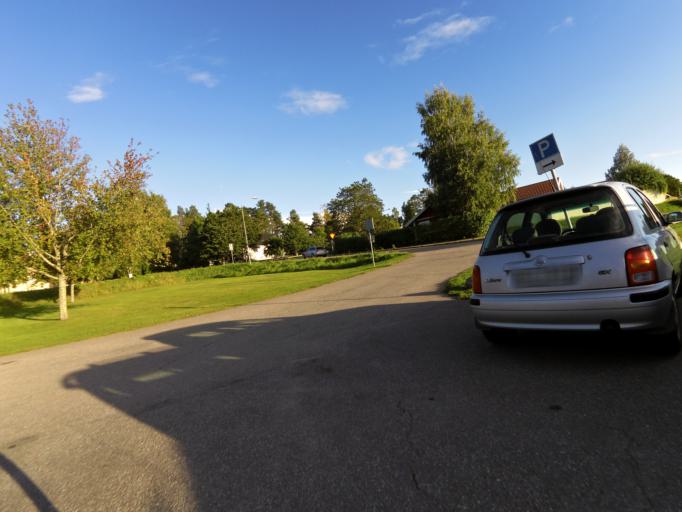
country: SE
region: Gaevleborg
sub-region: Gavle Kommun
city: Gavle
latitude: 60.7279
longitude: 17.1698
